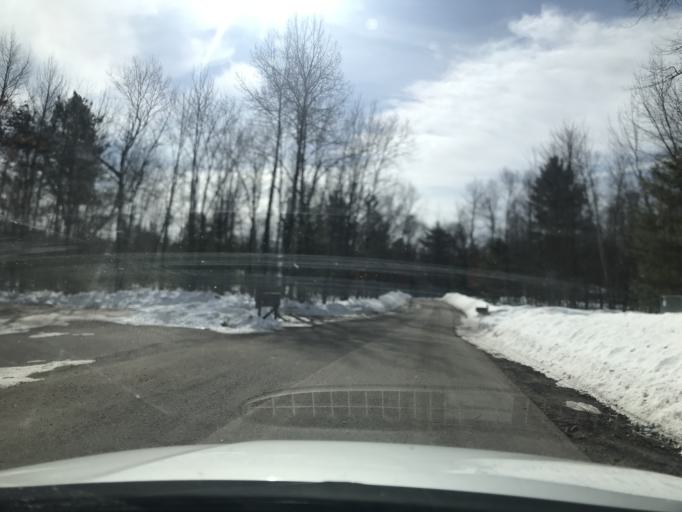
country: US
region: Wisconsin
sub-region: Menominee County
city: Legend Lake
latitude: 45.1152
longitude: -88.4439
